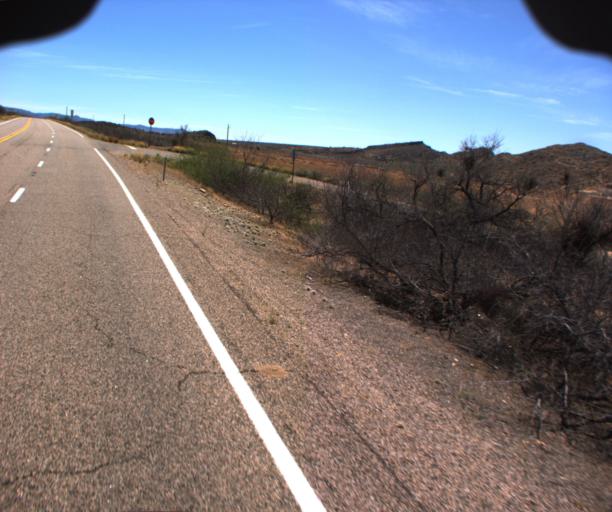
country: US
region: Arizona
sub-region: Mohave County
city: New Kingman-Butler
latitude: 35.3752
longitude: -113.7237
